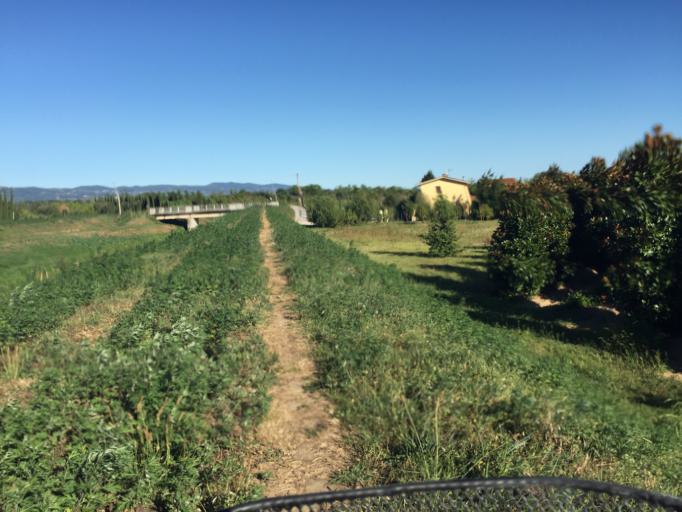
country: IT
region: Tuscany
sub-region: Provincia di Pistoia
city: Anchione
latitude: 43.8351
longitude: 10.7623
